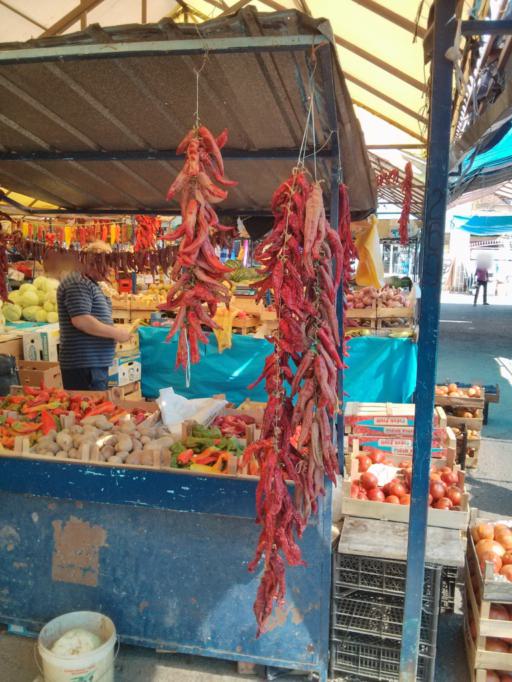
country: MK
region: Ohrid
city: Ohrid
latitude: 41.1171
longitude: 20.7995
